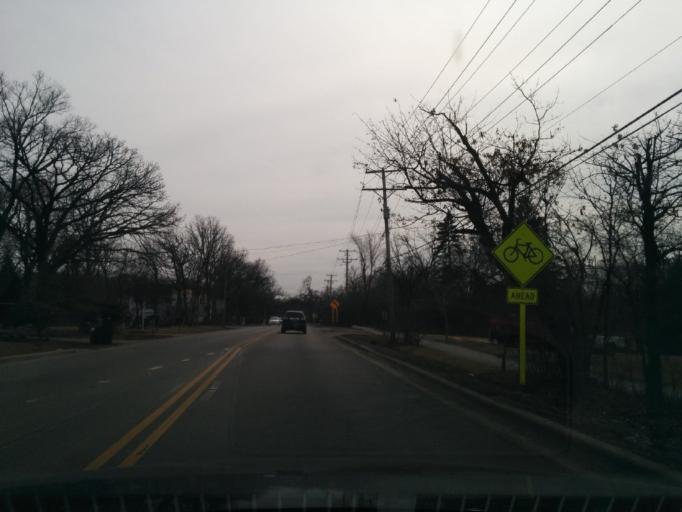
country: US
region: Illinois
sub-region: DuPage County
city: Oak Brook
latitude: 41.8311
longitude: -87.9286
